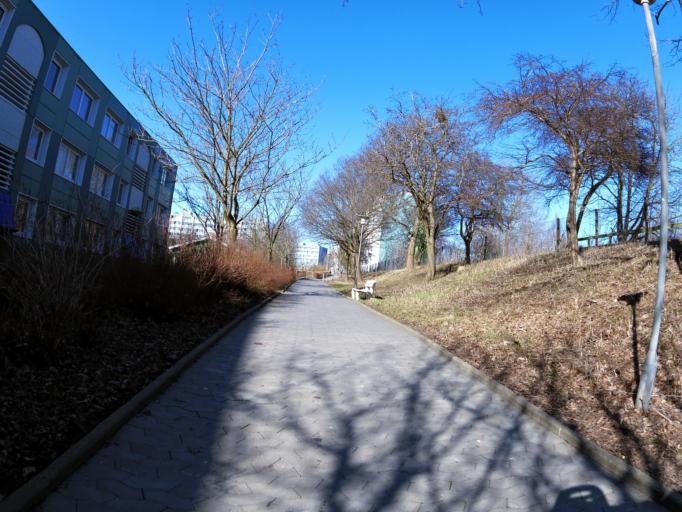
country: DK
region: Central Jutland
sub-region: Arhus Kommune
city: Arhus
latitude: 56.1684
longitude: 10.1748
